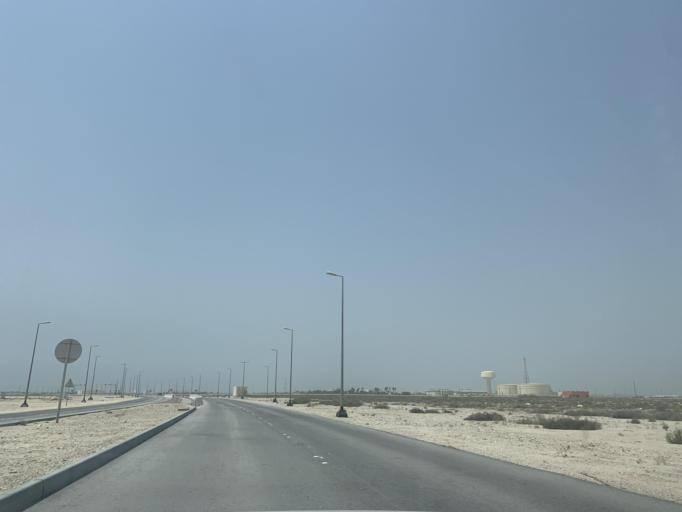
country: BH
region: Central Governorate
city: Dar Kulayb
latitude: 25.8433
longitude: 50.5934
